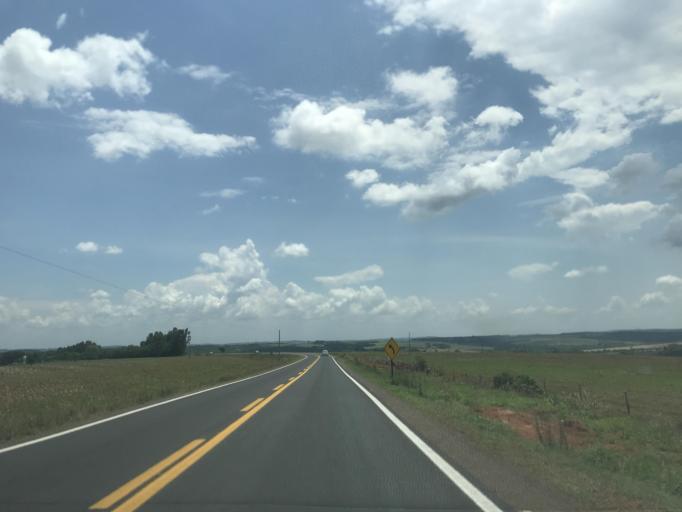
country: BR
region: Goias
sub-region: Bela Vista De Goias
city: Bela Vista de Goias
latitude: -17.1029
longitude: -48.6629
